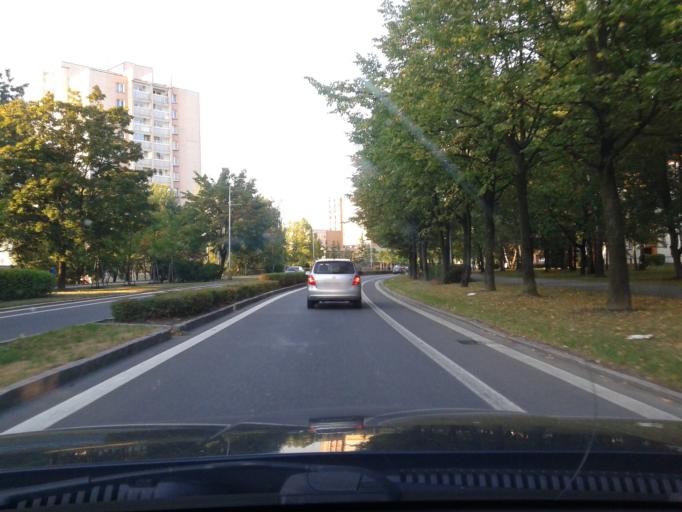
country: CZ
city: Dolni Lutyne
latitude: 49.8731
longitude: 18.4267
